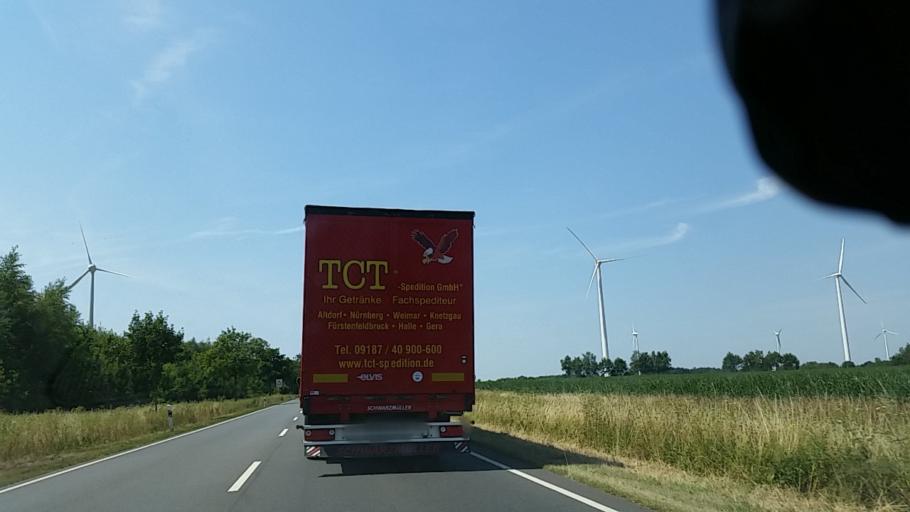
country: DE
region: Lower Saxony
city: Binnen
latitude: 52.6563
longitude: 9.1179
